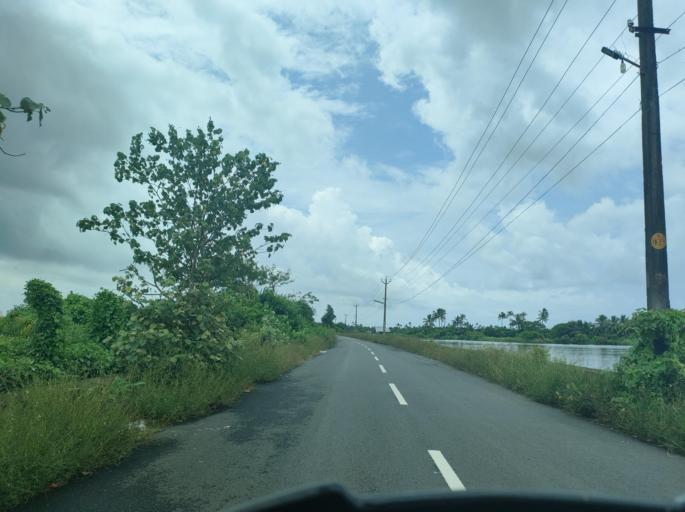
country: IN
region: Kerala
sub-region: Ernakulam
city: Elur
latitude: 10.0553
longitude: 76.2094
